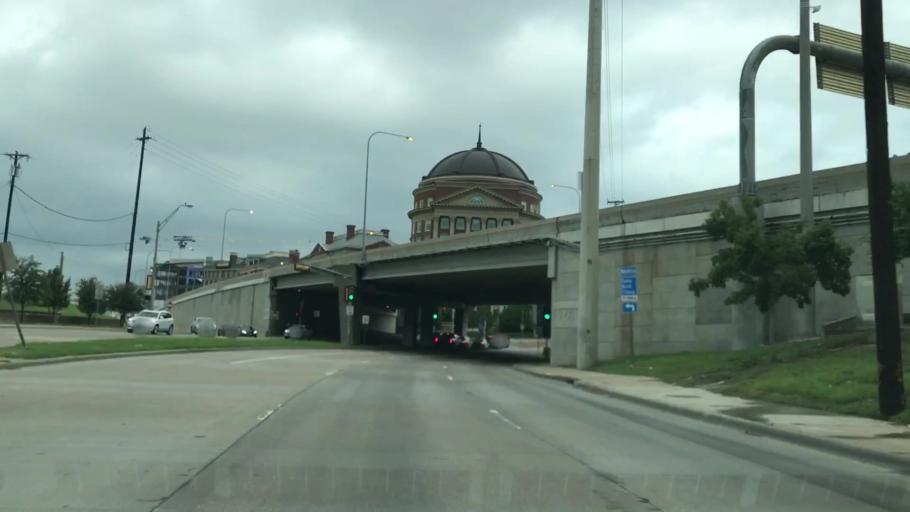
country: US
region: Texas
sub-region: Dallas County
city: Dallas
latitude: 32.8012
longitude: -96.8168
